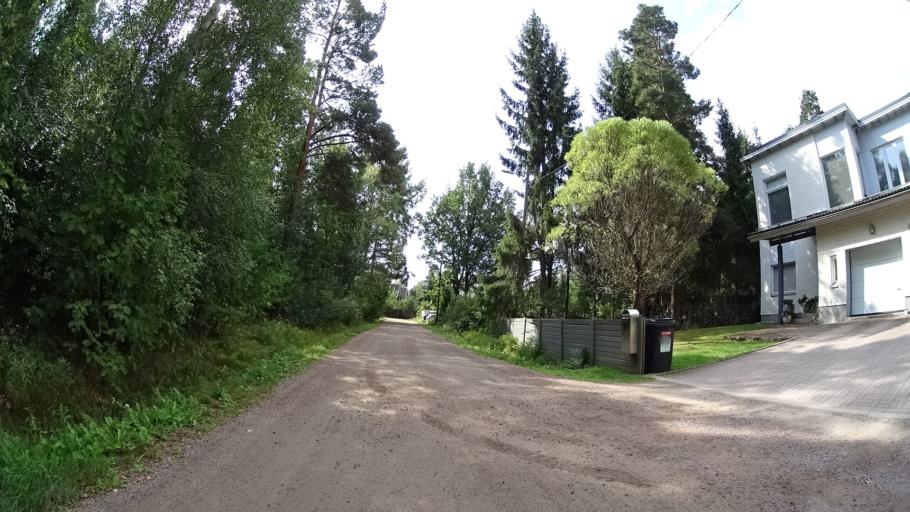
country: FI
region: Uusimaa
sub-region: Helsinki
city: Koukkuniemi
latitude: 60.1644
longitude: 24.7595
